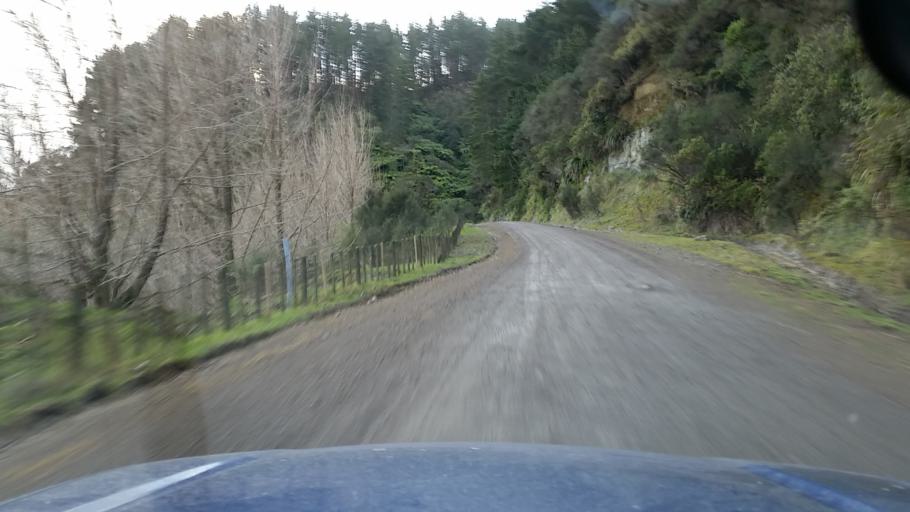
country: NZ
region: Taranaki
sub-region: South Taranaki District
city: Patea
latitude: -39.5565
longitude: 174.5699
